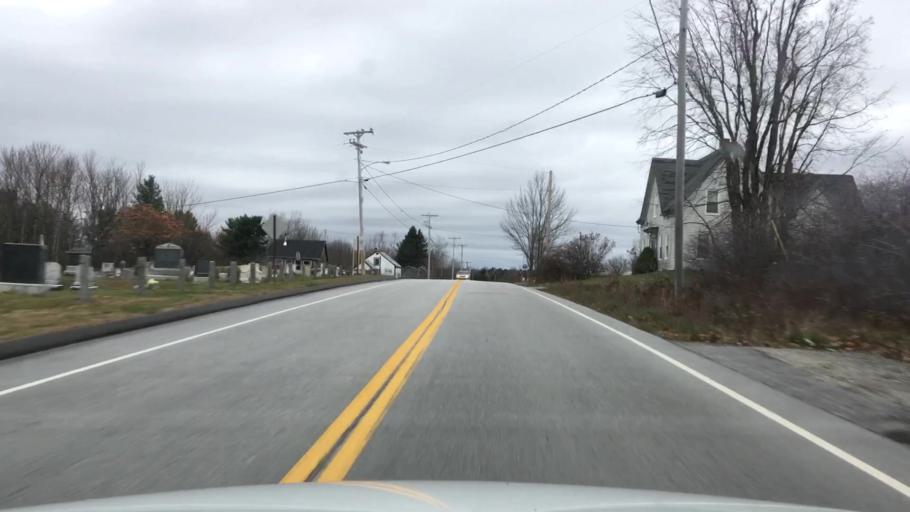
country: US
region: Maine
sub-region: Hancock County
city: Penobscot
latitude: 44.5215
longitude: -68.6605
